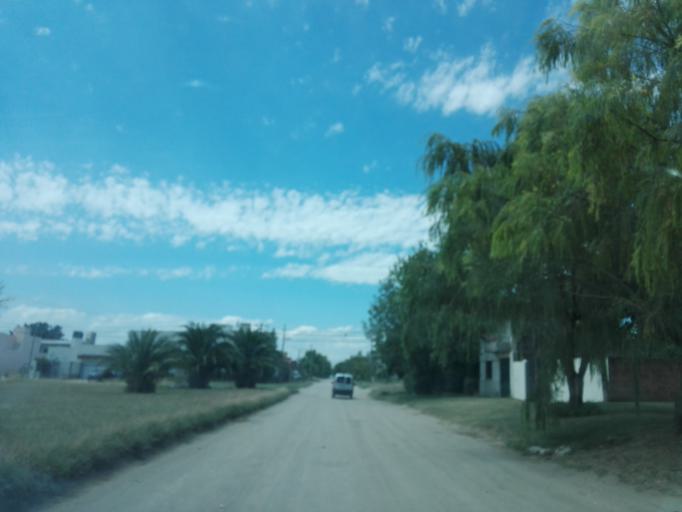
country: AR
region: Buenos Aires
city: Necochea
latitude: -38.5823
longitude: -58.7471
